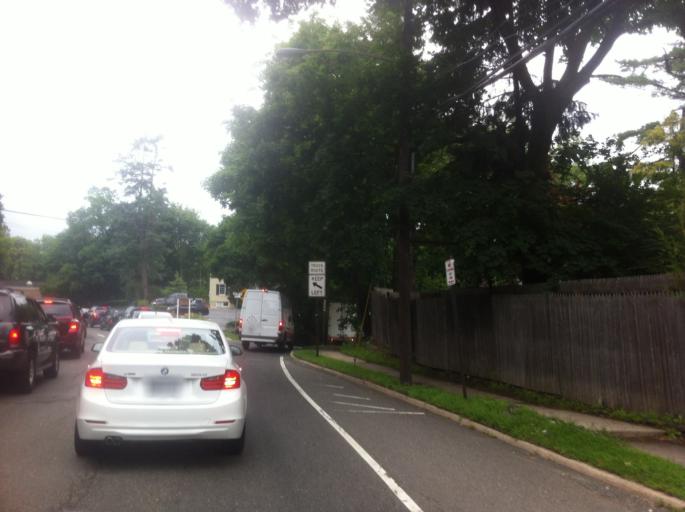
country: US
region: New York
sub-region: Nassau County
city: Roslyn Estates
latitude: 40.7991
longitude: -73.6579
